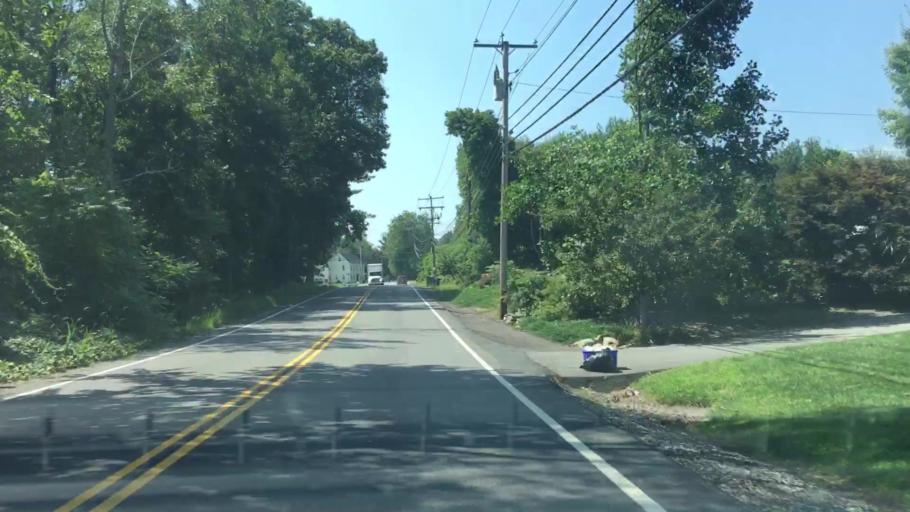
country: US
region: New Hampshire
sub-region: Rockingham County
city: Hampstead
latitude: 42.8785
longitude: -71.1688
